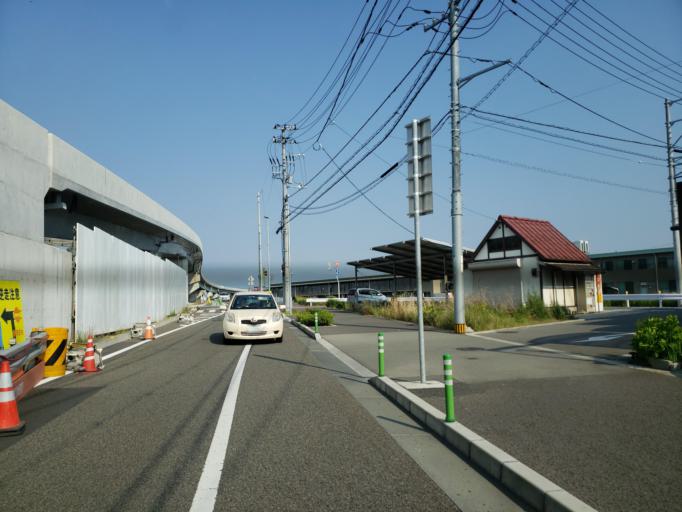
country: JP
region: Ehime
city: Masaki-cho
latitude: 33.8198
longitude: 132.7157
